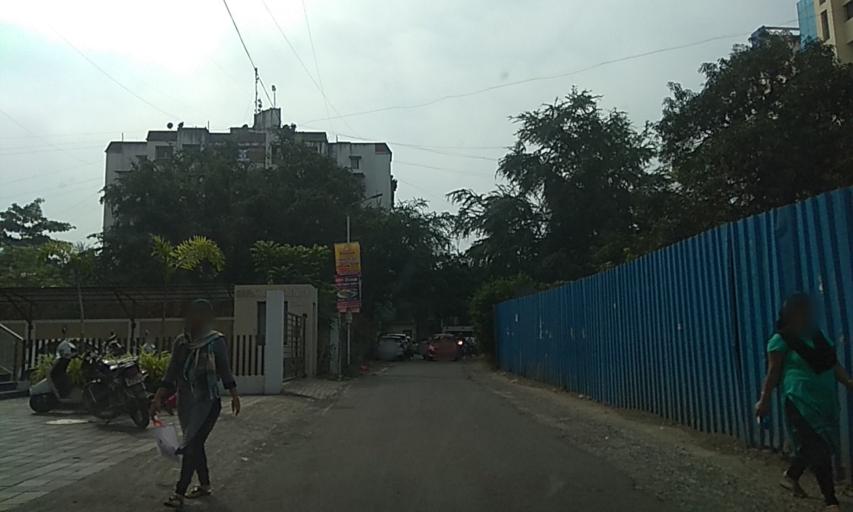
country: IN
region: Maharashtra
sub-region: Pune Division
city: Pune
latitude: 18.5038
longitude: 73.9296
